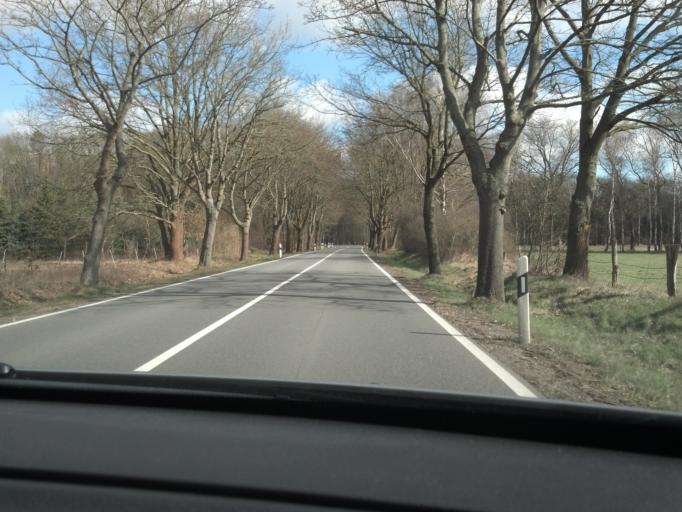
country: DE
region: Schleswig-Holstein
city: Langenlehsten
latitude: 53.4385
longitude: 10.7517
